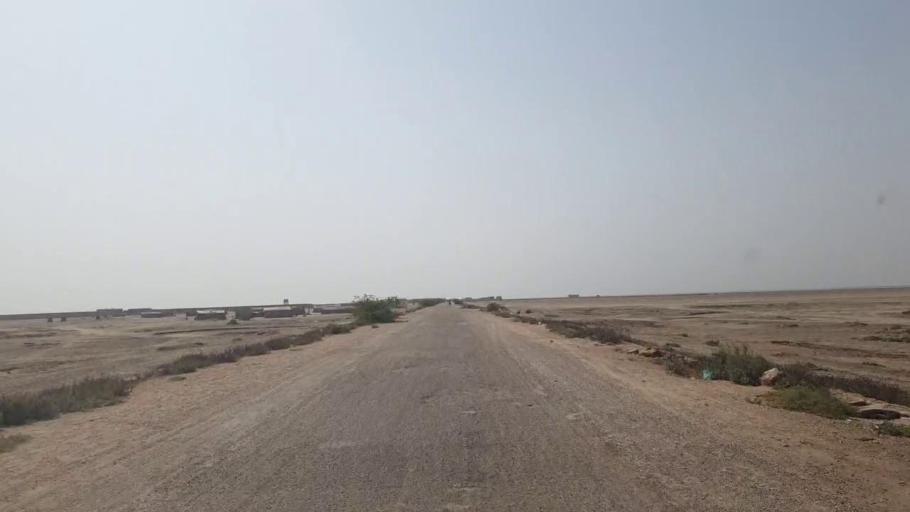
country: PK
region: Sindh
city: Jati
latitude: 24.3437
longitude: 68.5934
